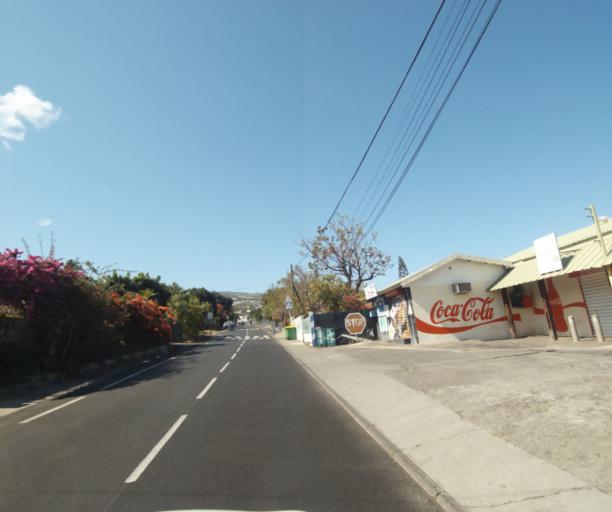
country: RE
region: Reunion
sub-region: Reunion
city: La Possession
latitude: -20.9790
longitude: 55.3240
